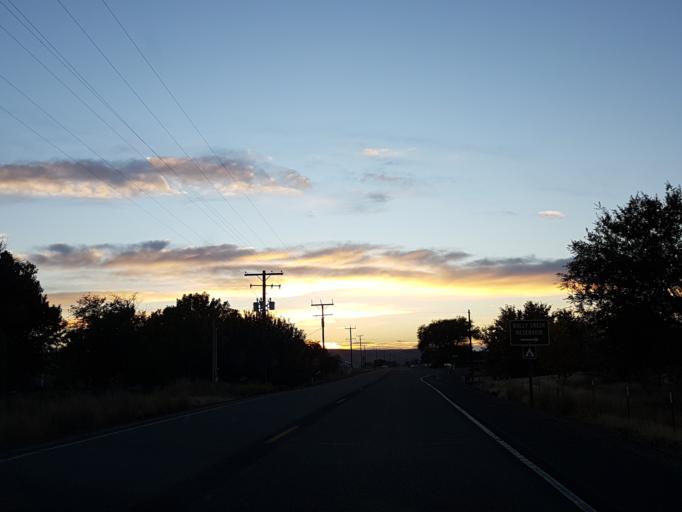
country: US
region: Oregon
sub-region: Malheur County
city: Vale
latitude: 43.9394
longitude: -117.3613
